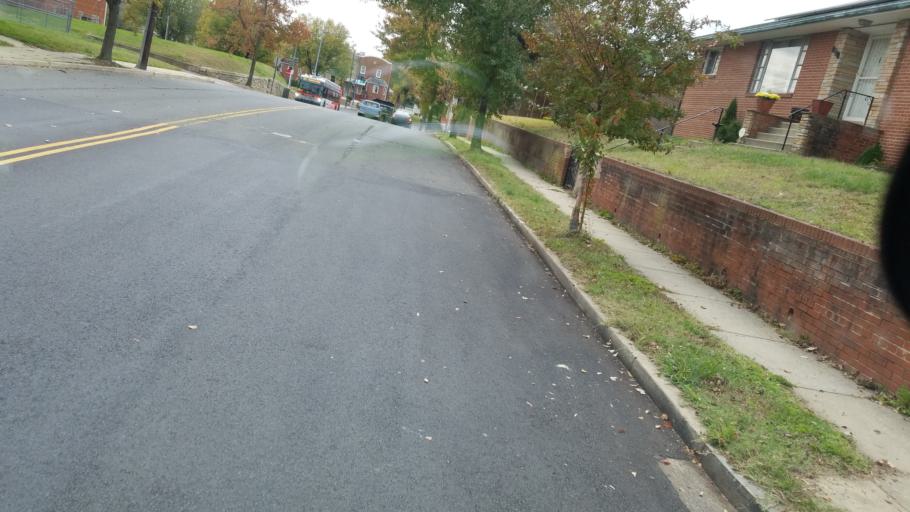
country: US
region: Maryland
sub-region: Prince George's County
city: Capitol Heights
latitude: 38.8909
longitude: -76.9280
